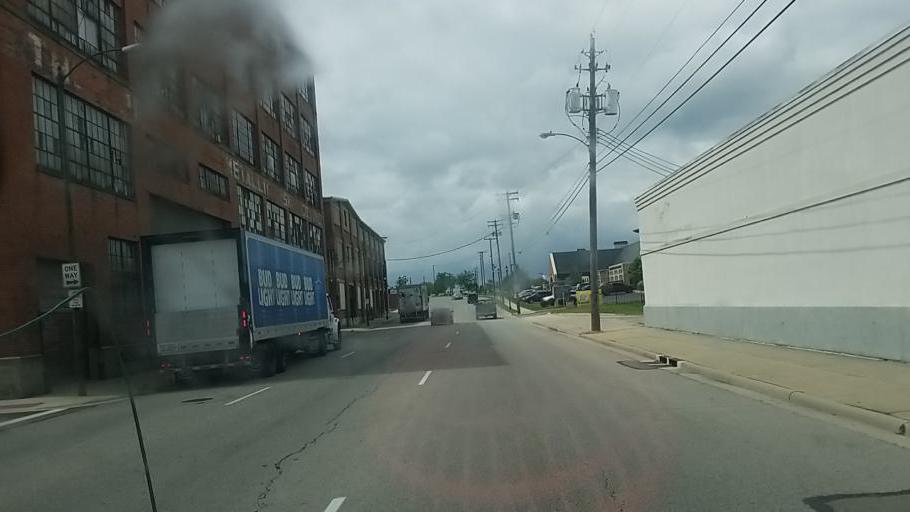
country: US
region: Ohio
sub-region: Clark County
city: Springfield
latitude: 39.9272
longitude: -83.8115
